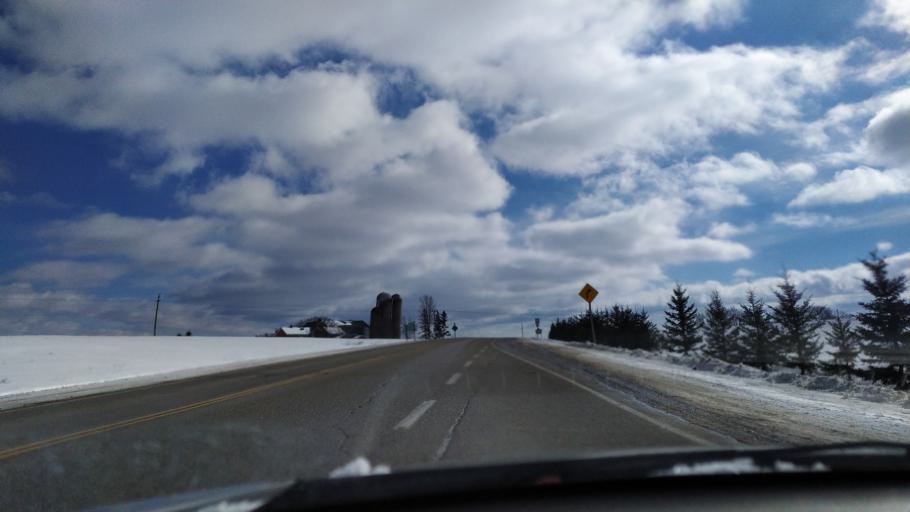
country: CA
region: Ontario
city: Waterloo
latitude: 43.5912
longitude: -80.6095
